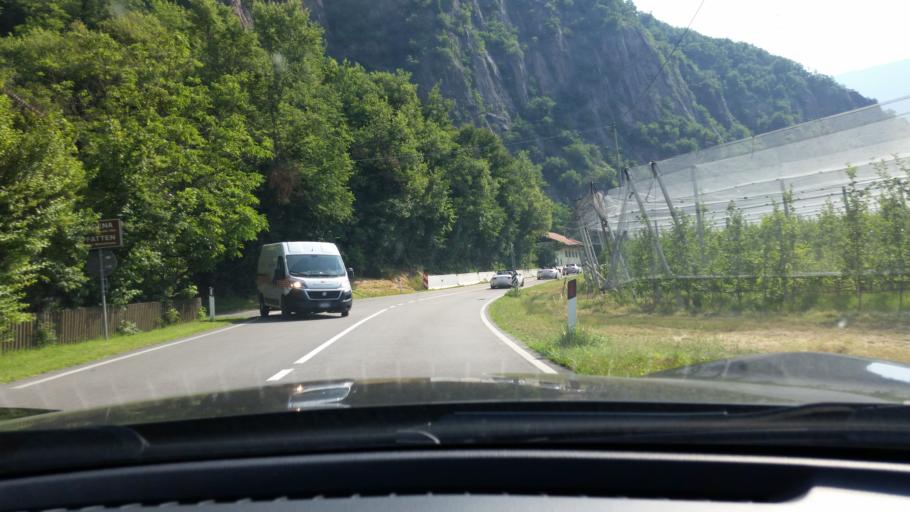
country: IT
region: Trentino-Alto Adige
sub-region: Bolzano
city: Ora
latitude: 46.3545
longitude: 11.2812
